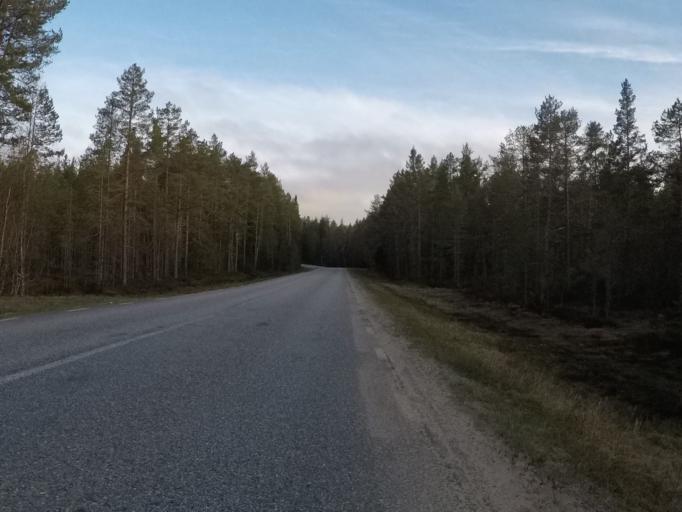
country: SE
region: Vaesterbotten
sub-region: Robertsfors Kommun
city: Robertsfors
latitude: 63.9823
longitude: 20.8112
